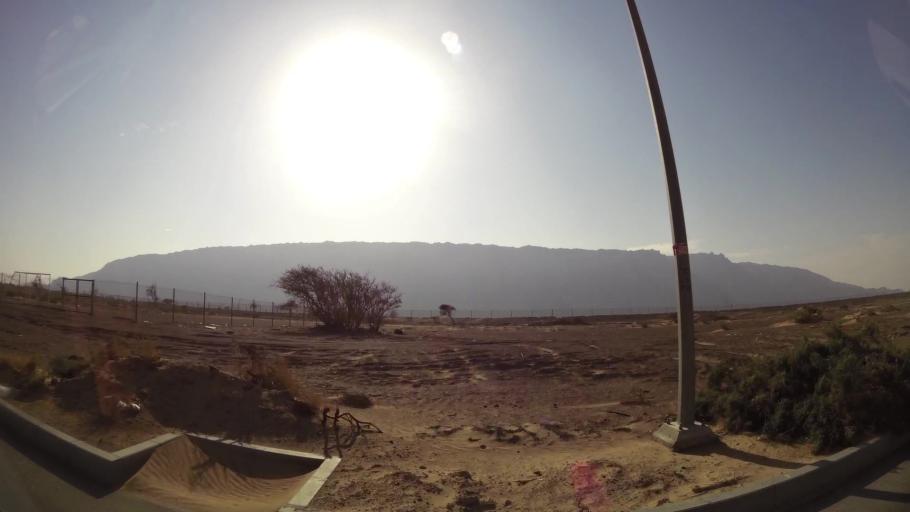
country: AE
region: Abu Dhabi
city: Al Ain
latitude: 24.0372
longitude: 55.8382
